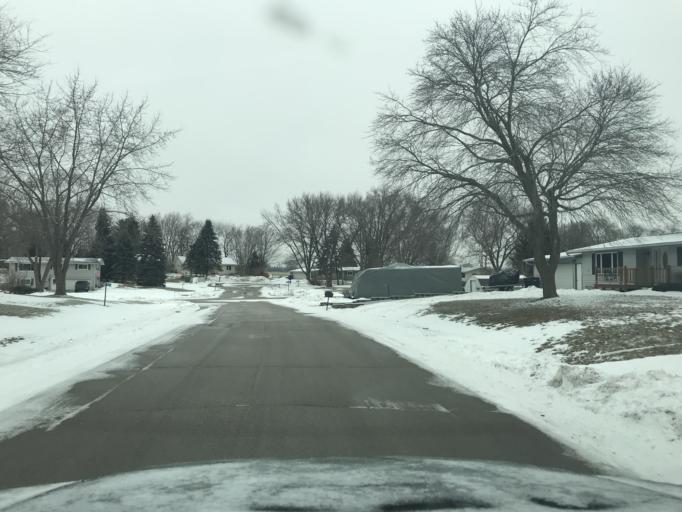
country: US
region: Wisconsin
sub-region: Dane County
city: Cottage Grove
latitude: 43.0988
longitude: -89.2358
